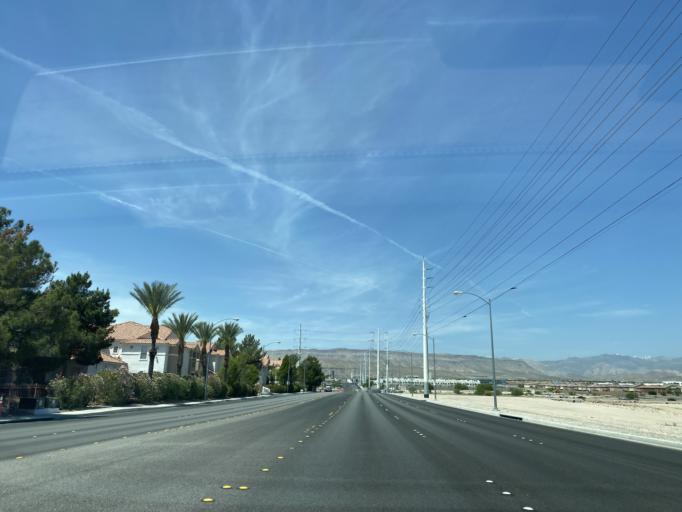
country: US
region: Nevada
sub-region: Clark County
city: Spring Valley
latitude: 36.0852
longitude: -115.2754
